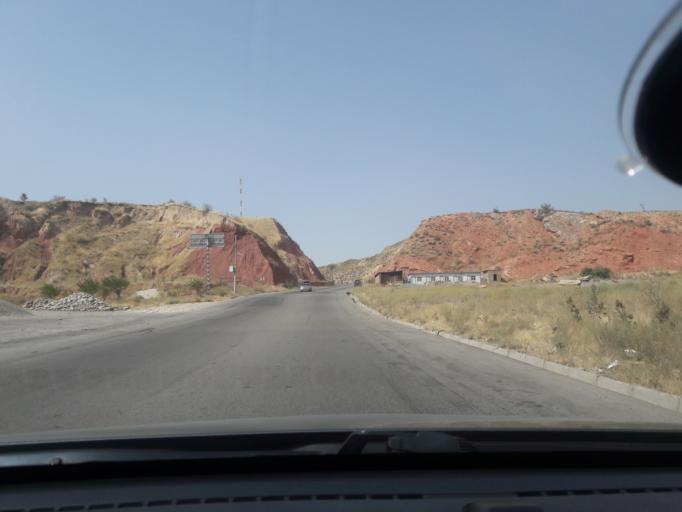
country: TJ
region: Republican Subordination
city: Vahdat
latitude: 38.4880
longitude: 69.1756
